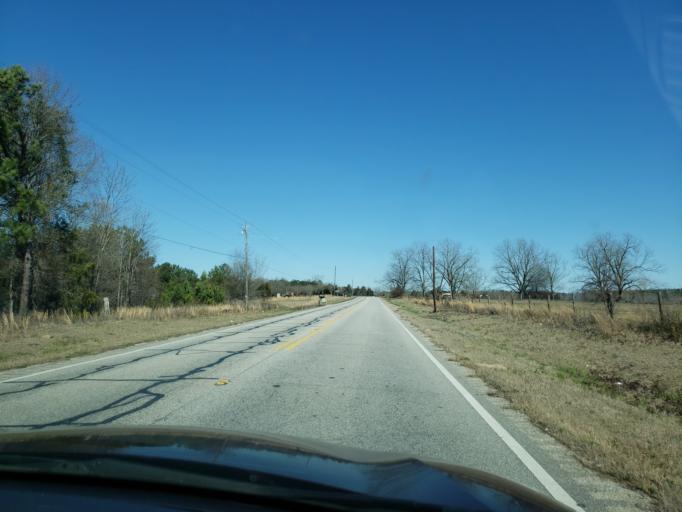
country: US
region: Alabama
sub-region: Macon County
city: Tuskegee
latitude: 32.5830
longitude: -85.6515
